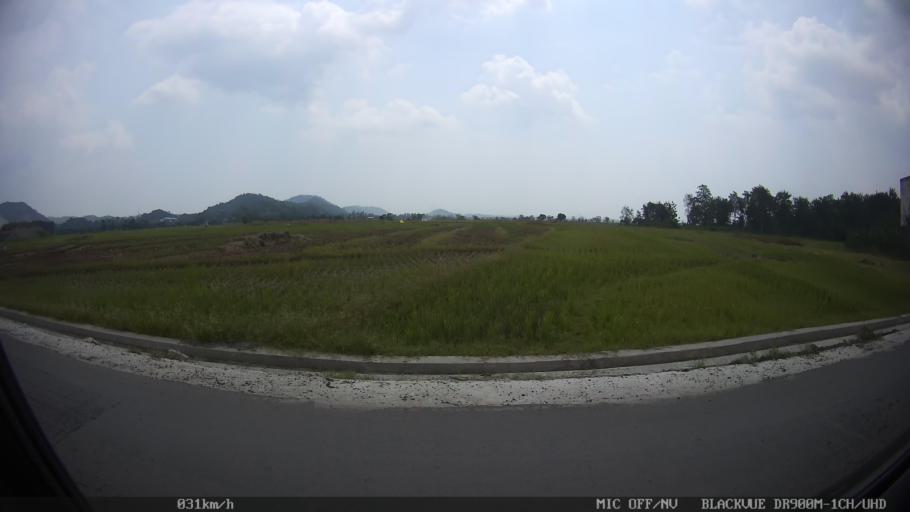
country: ID
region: Lampung
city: Gadingrejo
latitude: -5.3692
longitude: 105.0269
